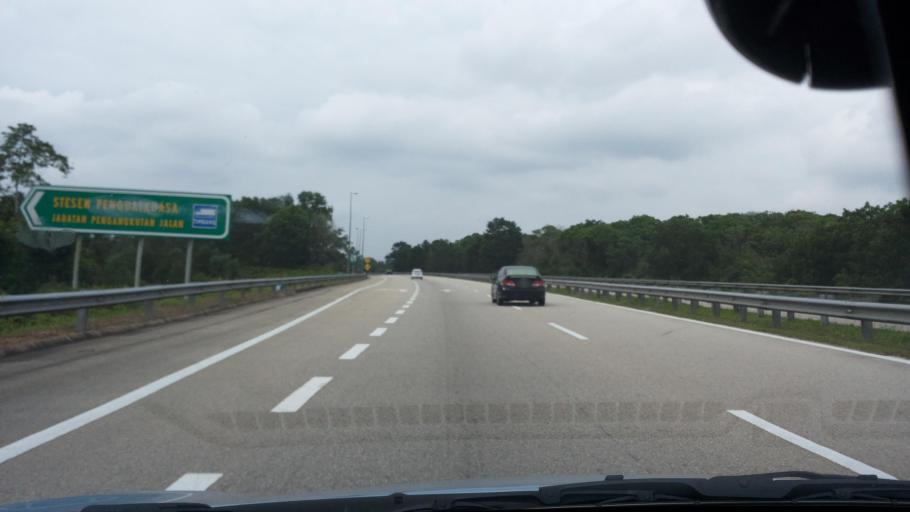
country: MY
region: Pahang
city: Kuantan
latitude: 3.8480
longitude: 103.2242
